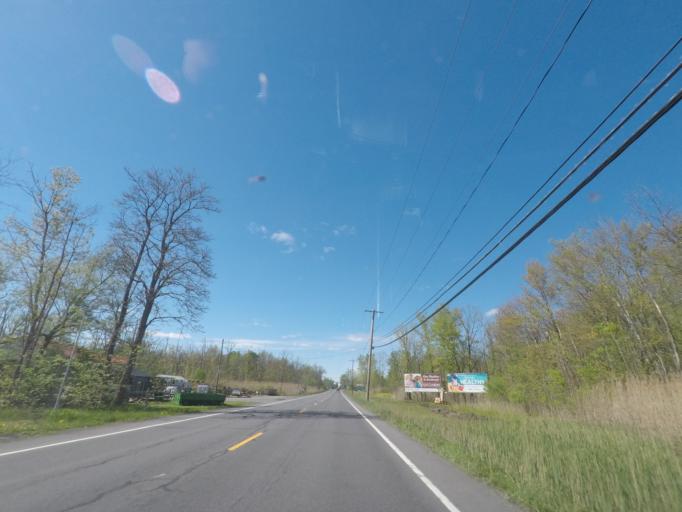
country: US
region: New York
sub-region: Rensselaer County
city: Castleton-on-Hudson
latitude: 42.5453
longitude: -73.8068
